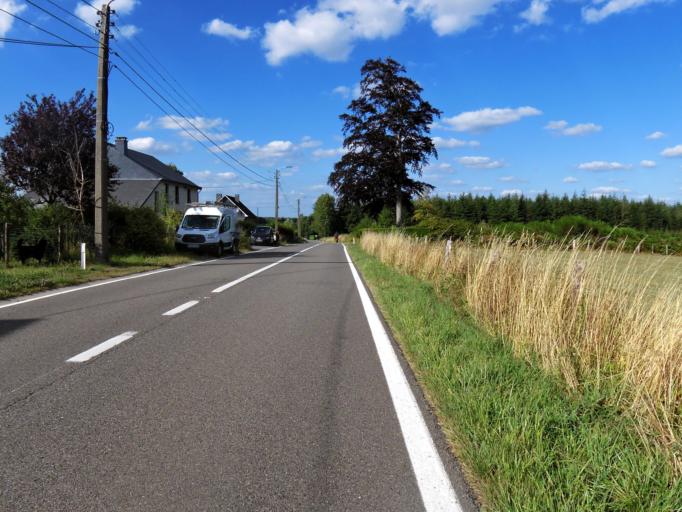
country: BE
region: Wallonia
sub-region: Province de Namur
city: Bievre
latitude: 49.9275
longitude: 5.0420
